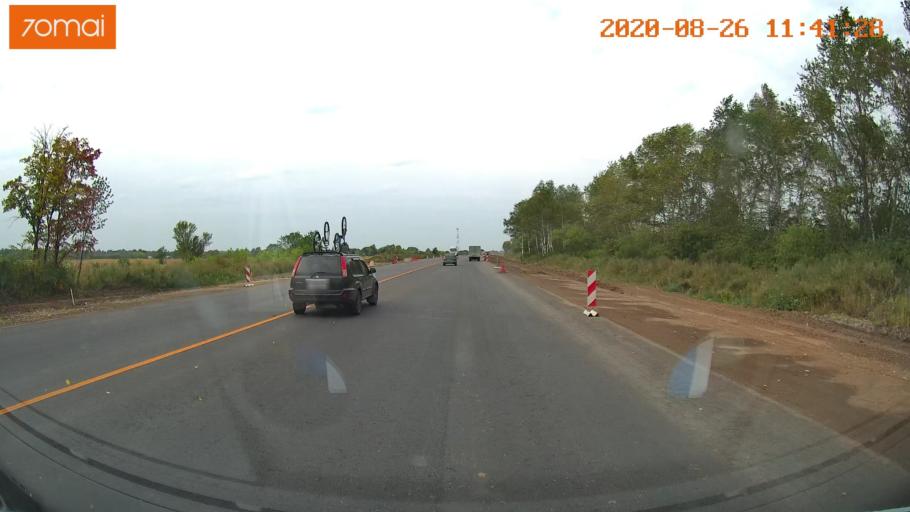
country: RU
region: Rjazan
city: Shilovo
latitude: 54.2953
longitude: 40.7111
